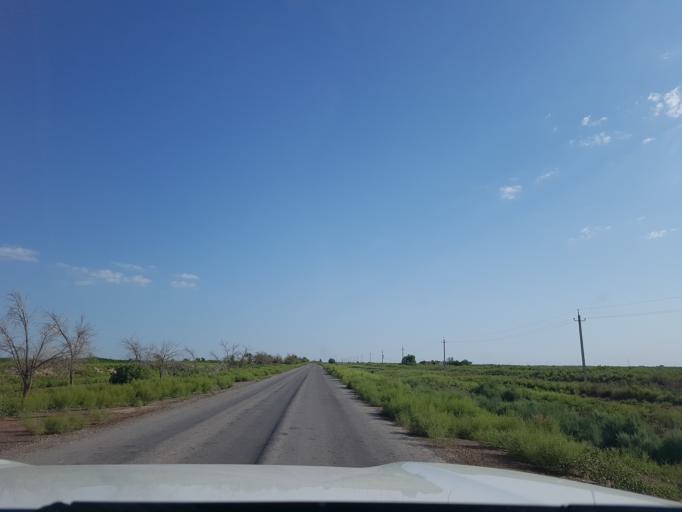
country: TM
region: Dasoguz
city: Koeneuergench
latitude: 41.8919
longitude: 58.7070
